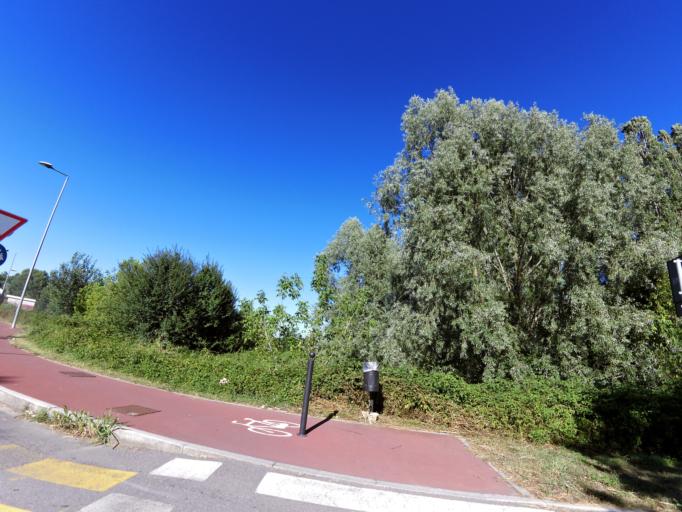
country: IT
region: Lombardy
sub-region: Citta metropolitana di Milano
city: Bettola-Zeloforomagno
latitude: 45.4223
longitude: 9.2977
